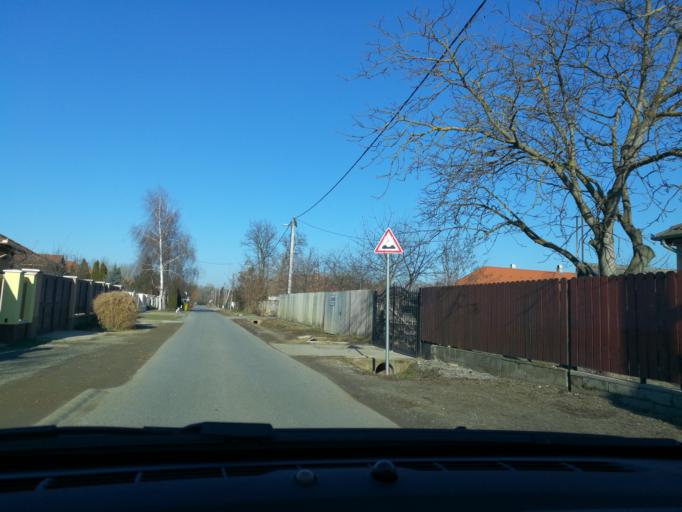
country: HU
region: Szabolcs-Szatmar-Bereg
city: Nyiregyhaza
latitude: 47.9461
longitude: 21.7470
